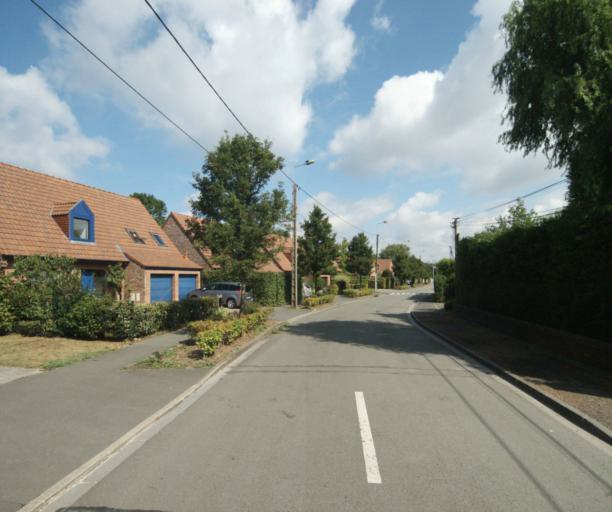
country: FR
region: Nord-Pas-de-Calais
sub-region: Departement du Nord
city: Wasquehal
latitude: 50.6543
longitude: 3.1493
